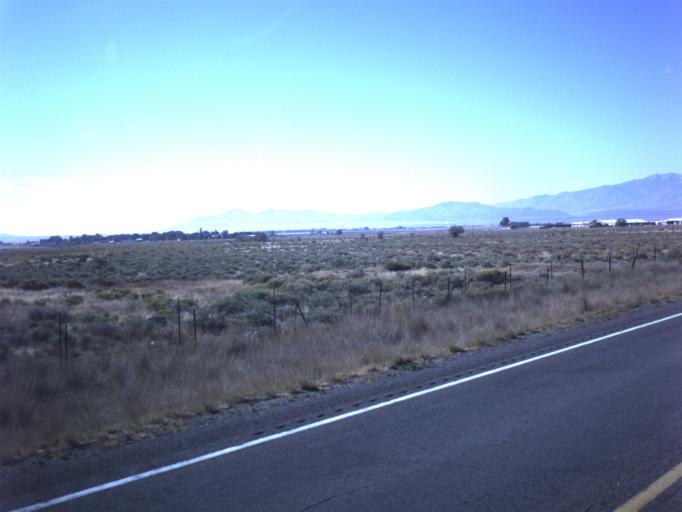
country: US
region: Utah
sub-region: Tooele County
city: Erda
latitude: 40.6226
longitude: -112.3550
